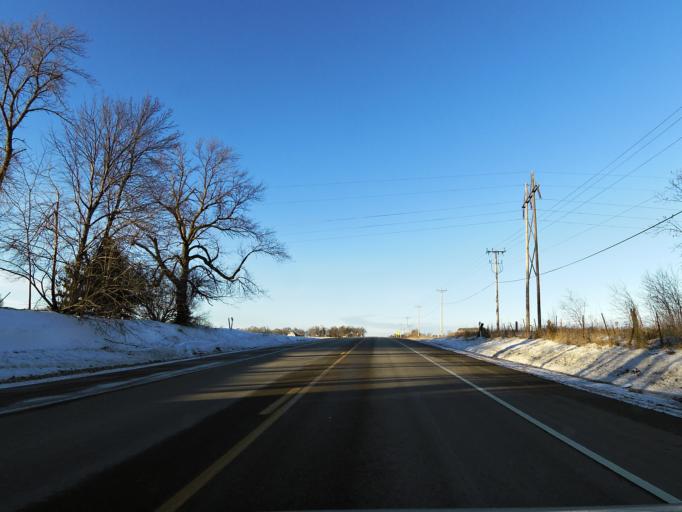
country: US
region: Minnesota
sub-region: Washington County
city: Cottage Grove
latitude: 44.8832
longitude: -92.9033
